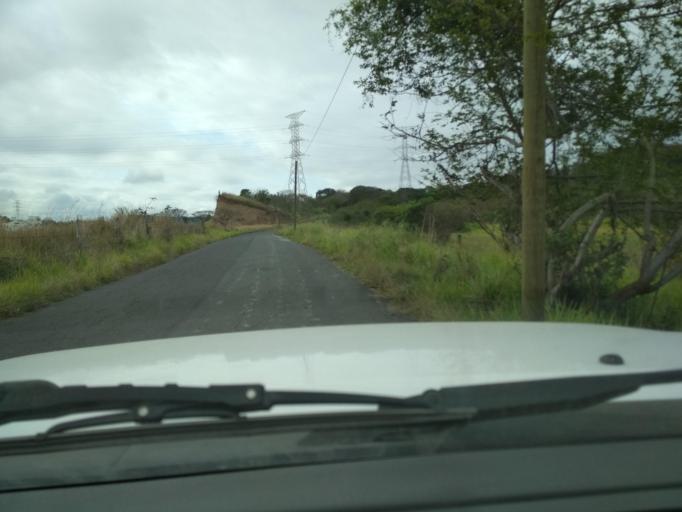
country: MX
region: Veracruz
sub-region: Medellin
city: Fraccionamiento Arboledas San Ramon
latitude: 19.0886
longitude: -96.1361
